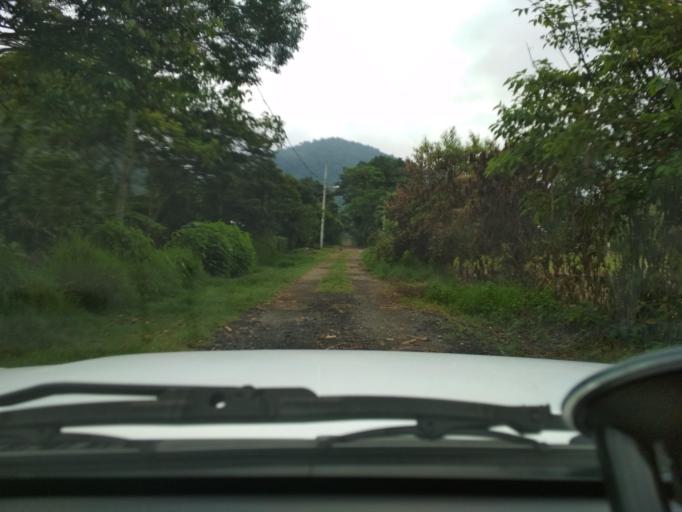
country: MX
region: Veracruz
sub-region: Ixtaczoquitlan
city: Buenavista
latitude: 18.9202
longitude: -97.0476
